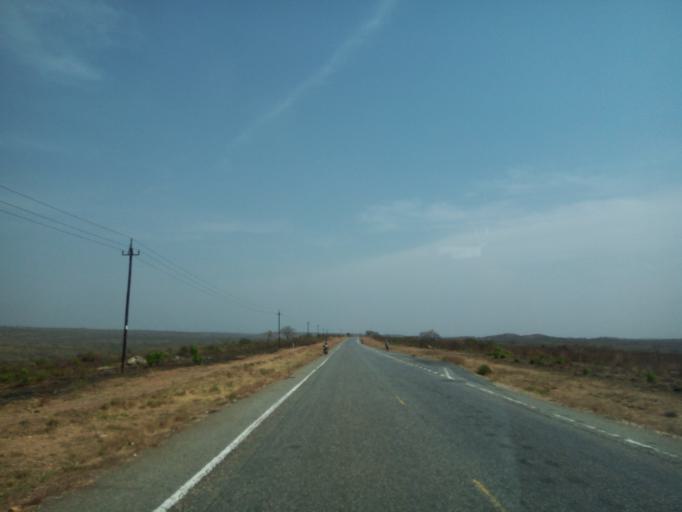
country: UG
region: Northern Region
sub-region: Nebbi District
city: Nebbi
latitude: 2.4387
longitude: 31.2511
